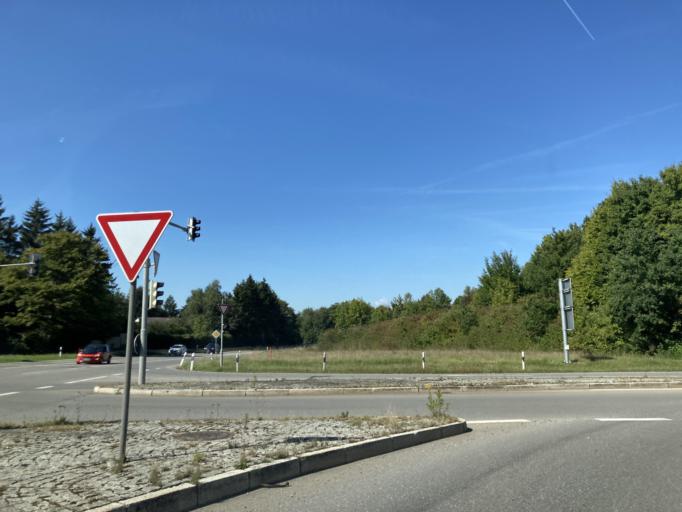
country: DE
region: Baden-Wuerttemberg
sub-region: Tuebingen Region
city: Riedlingen
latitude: 48.1528
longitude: 9.4955
